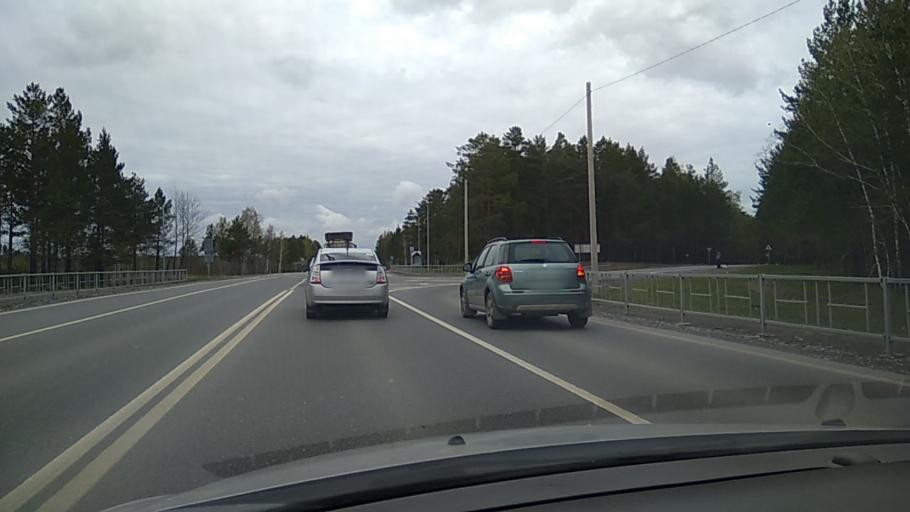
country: RU
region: Tjumen
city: Chervishevo
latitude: 56.9986
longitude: 65.4822
